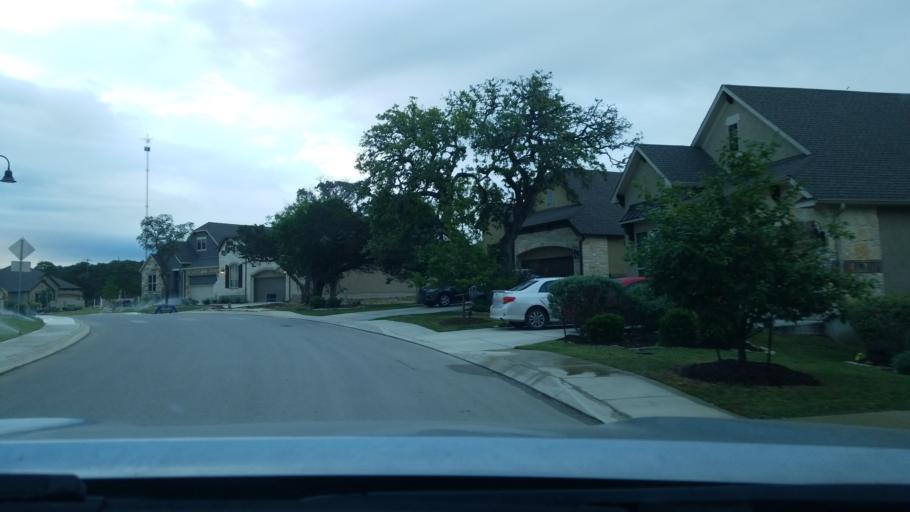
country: US
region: Texas
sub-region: Bexar County
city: Timberwood Park
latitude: 29.7158
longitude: -98.4595
